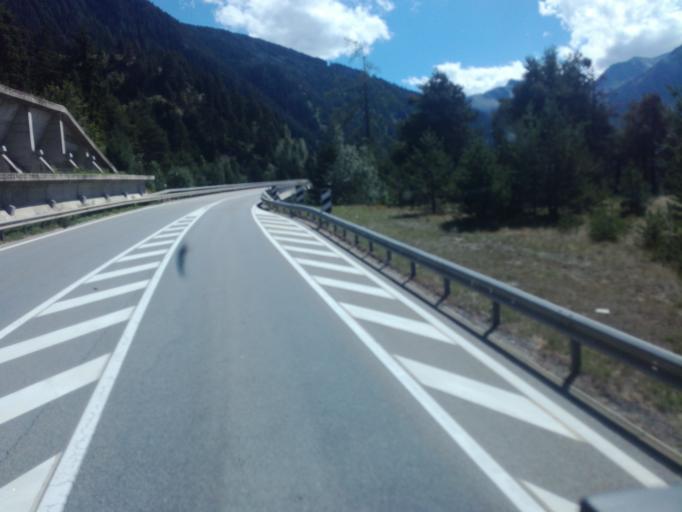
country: CH
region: Valais
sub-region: Brig District
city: Naters
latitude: 46.3250
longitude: 8.0330
